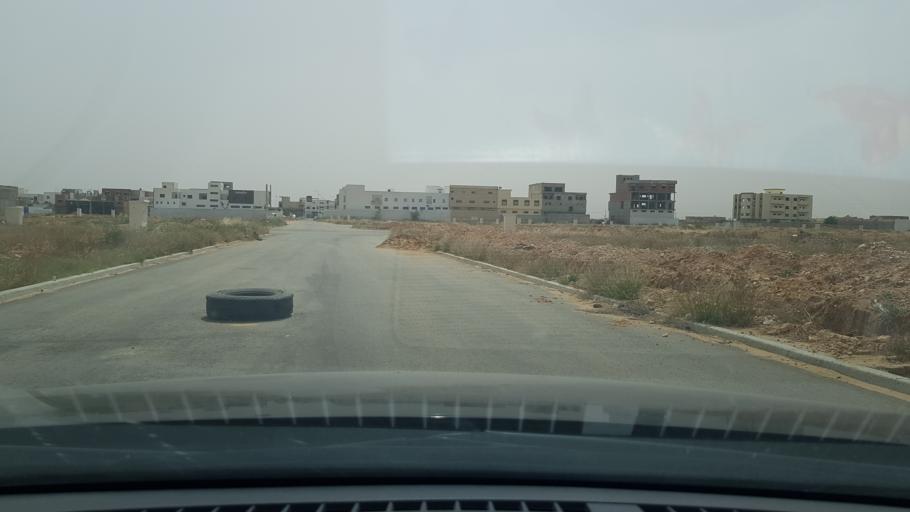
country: TN
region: Safaqis
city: Al Qarmadah
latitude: 34.8285
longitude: 10.7429
